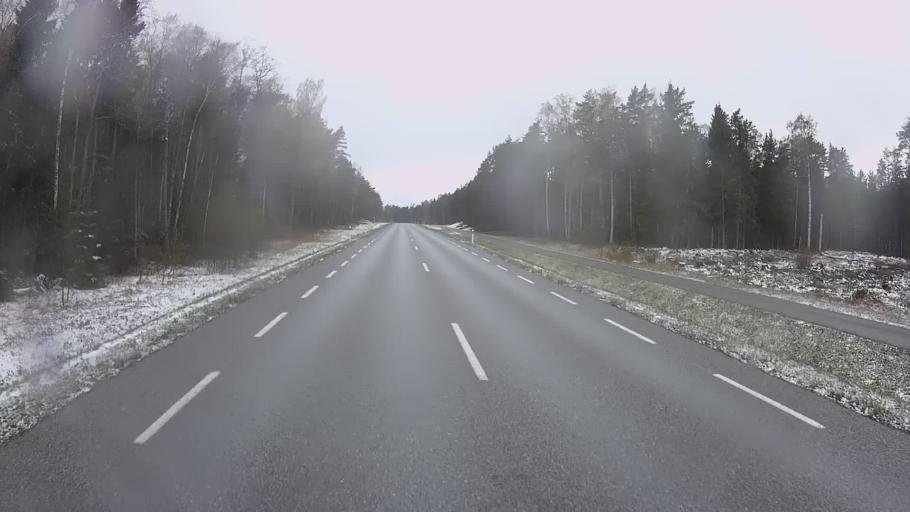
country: EE
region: Hiiumaa
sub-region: Kaerdla linn
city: Kardla
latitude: 59.0102
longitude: 22.6422
